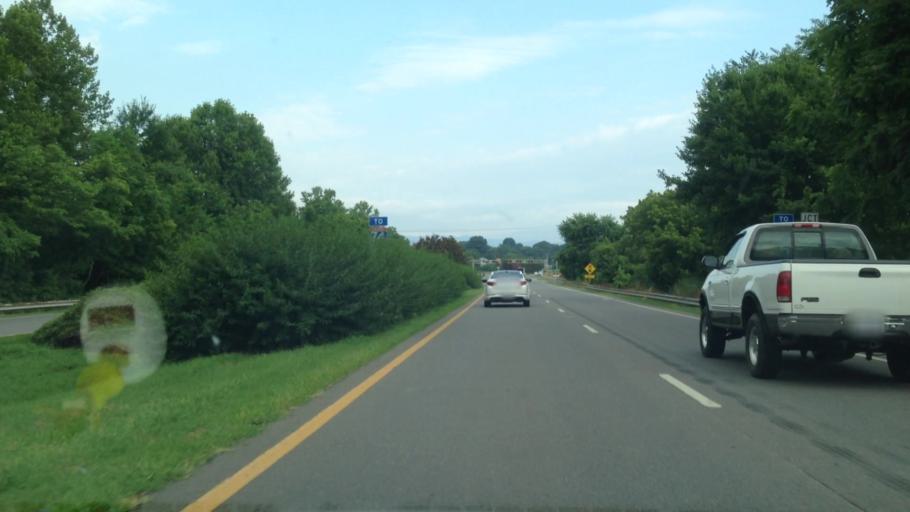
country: US
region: North Carolina
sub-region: Surry County
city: Mount Airy
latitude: 36.4831
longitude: -80.6089
